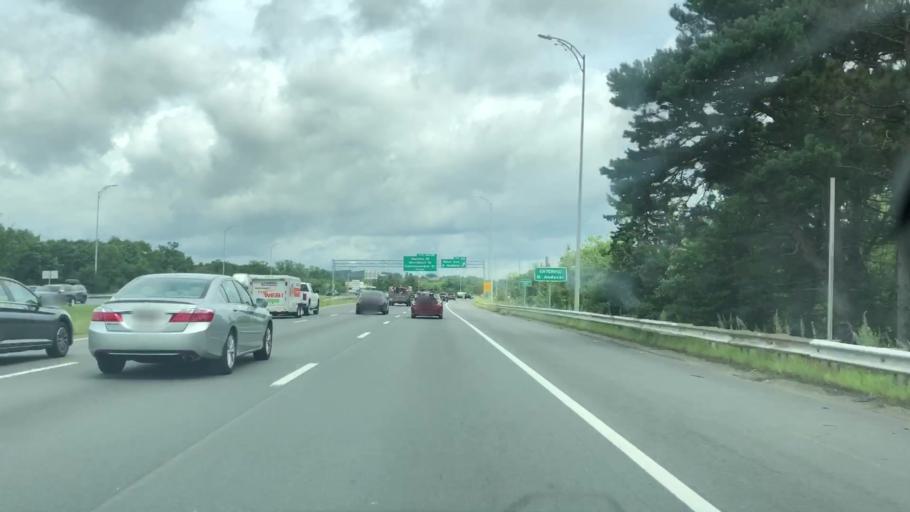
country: US
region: Massachusetts
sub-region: Essex County
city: North Andover
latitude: 42.6934
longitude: -71.1417
